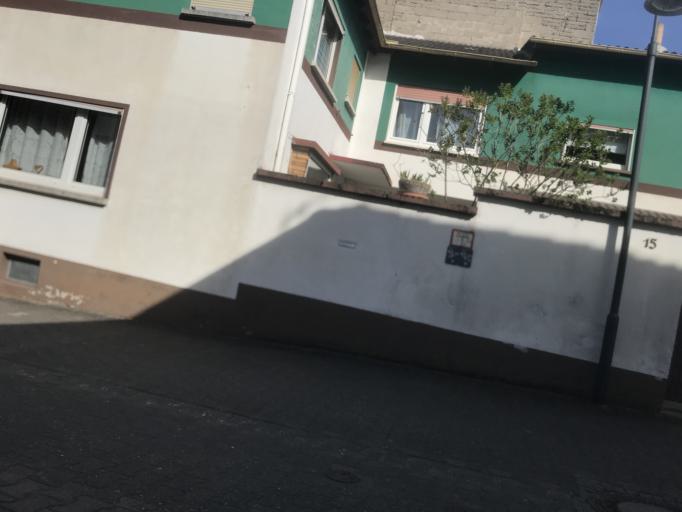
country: DE
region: Rheinland-Pfalz
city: Stadecken-Elsheim
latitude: 49.9133
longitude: 8.1351
